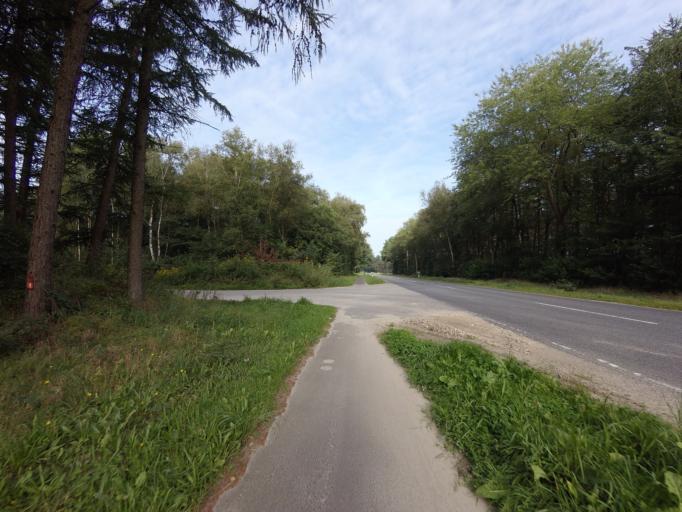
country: DE
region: Lower Saxony
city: Itterbeck
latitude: 52.5157
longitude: 6.7662
